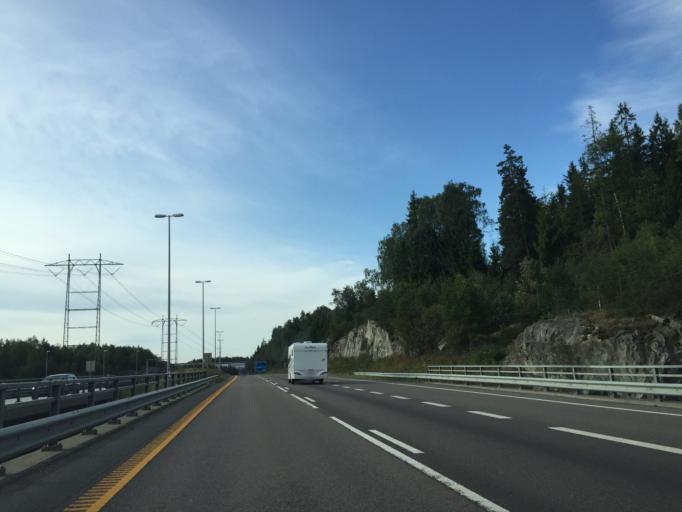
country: NO
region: Akershus
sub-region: Oppegard
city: Kolbotn
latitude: 59.7843
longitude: 10.8389
